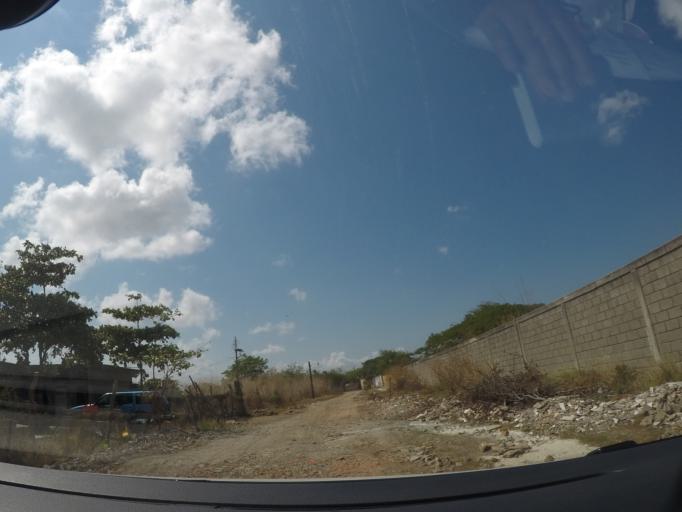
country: MX
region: Oaxaca
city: Juchitan de Zaragoza
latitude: 16.4377
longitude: -95.0087
